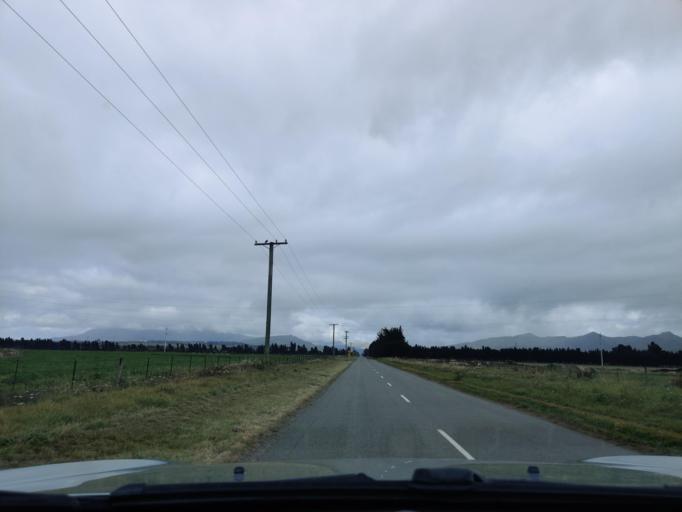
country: NZ
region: Canterbury
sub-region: Hurunui District
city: Amberley
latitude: -43.0773
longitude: 172.7228
